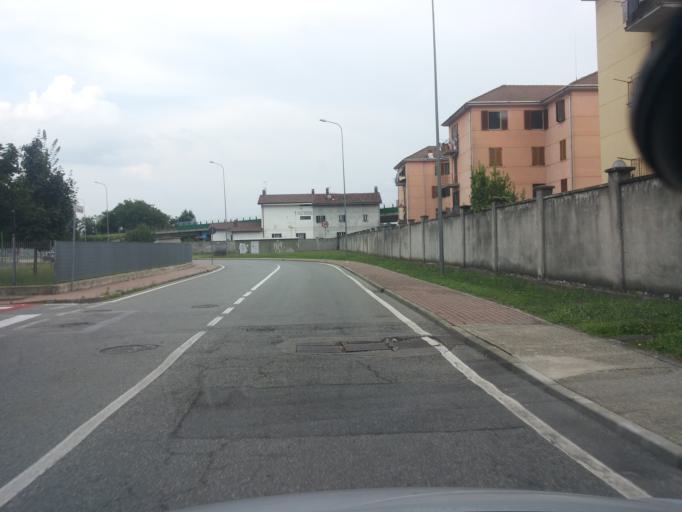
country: IT
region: Piedmont
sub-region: Provincia di Torino
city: Ivrea
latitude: 45.4583
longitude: 7.8802
